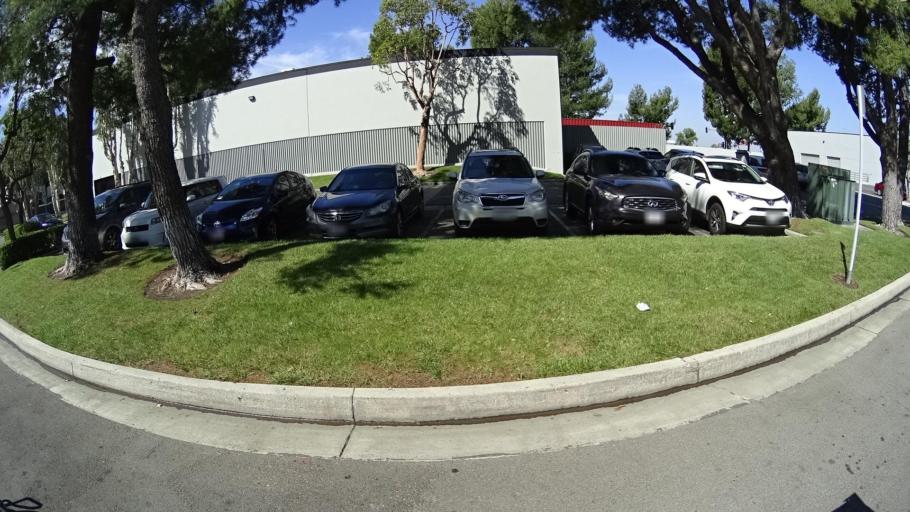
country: US
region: California
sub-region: Los Angeles County
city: Walnut
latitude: 33.9951
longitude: -117.8688
